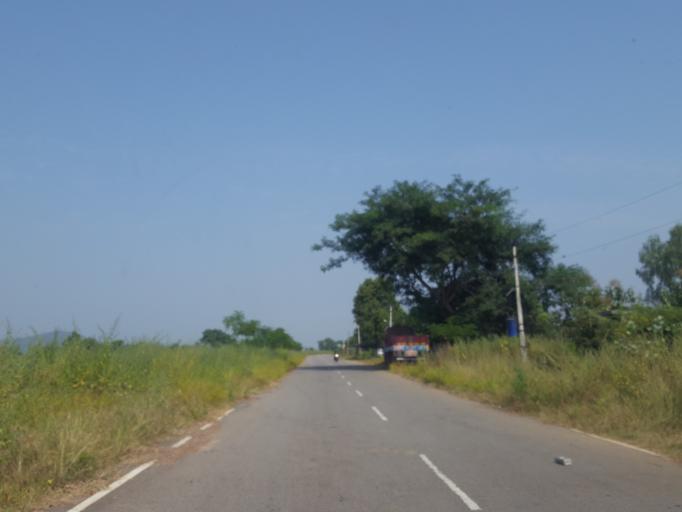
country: IN
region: Telangana
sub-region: Khammam
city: Yellandu
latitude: 17.6600
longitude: 80.2767
